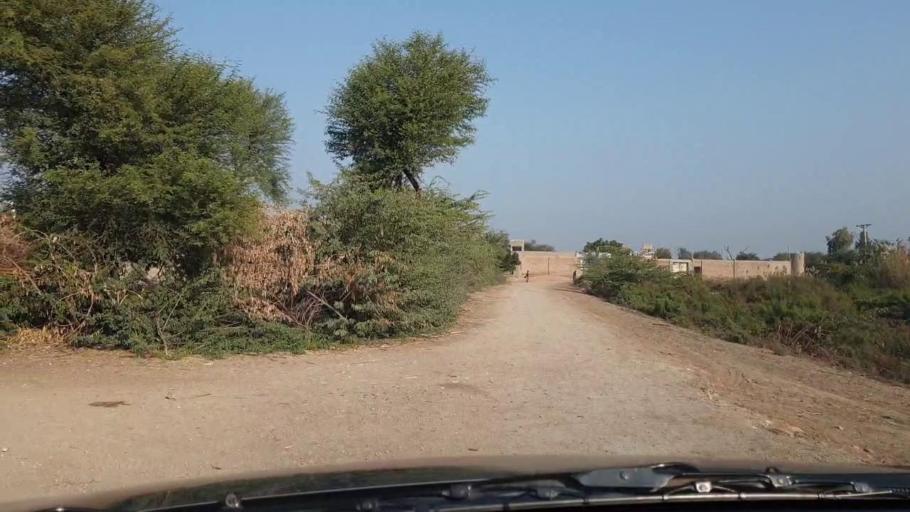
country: PK
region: Sindh
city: Sanghar
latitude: 25.9850
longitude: 68.9518
